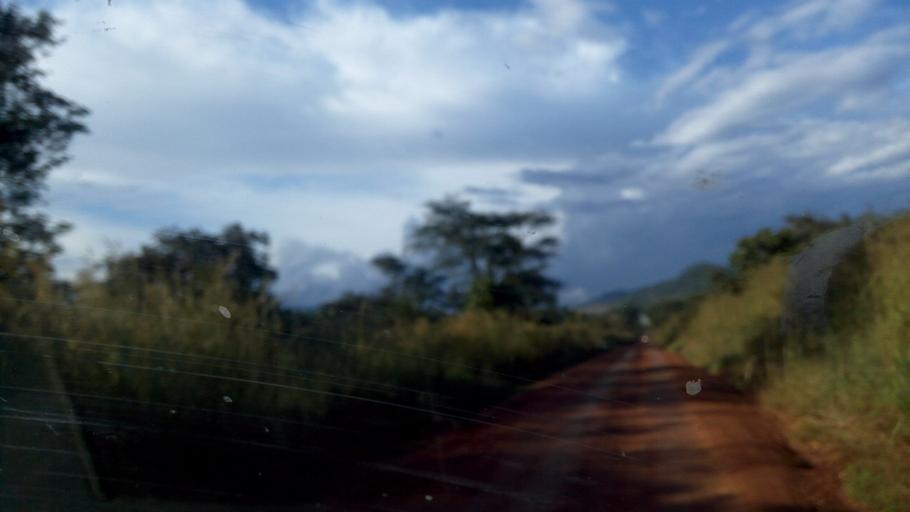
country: TZ
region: Kigoma
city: Kigoma
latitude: -4.6353
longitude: 28.7747
